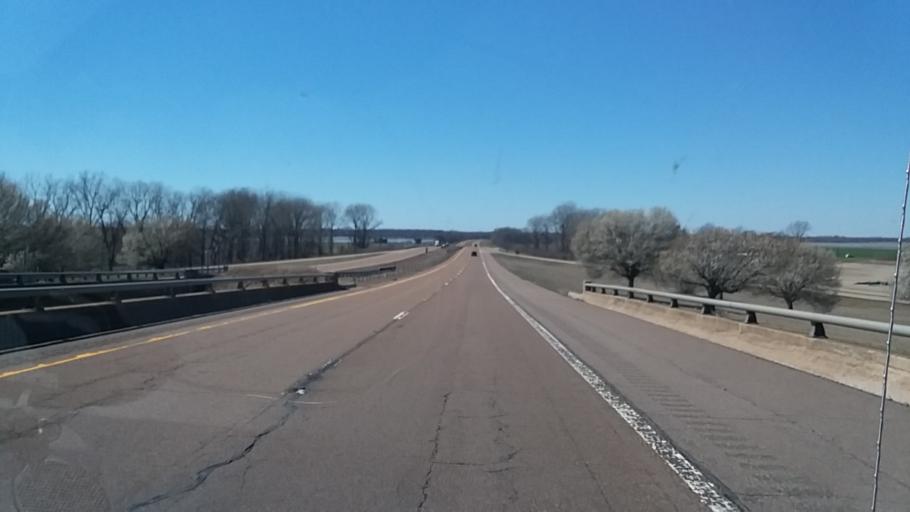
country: US
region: Tennessee
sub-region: Dyer County
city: Dyersburg
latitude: 36.0757
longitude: -89.4967
